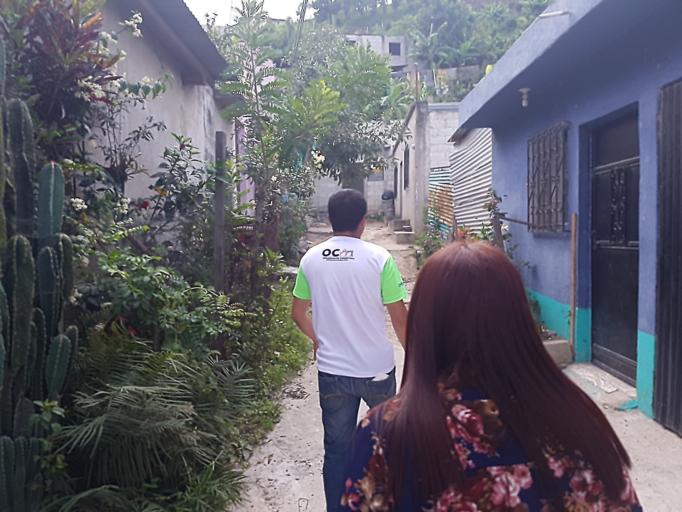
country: GT
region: Guatemala
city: Petapa
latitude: 14.5024
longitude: -90.5545
